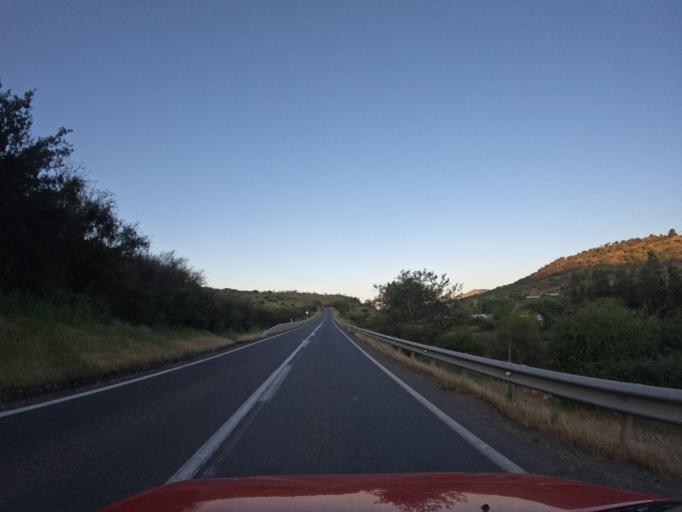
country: CL
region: Maule
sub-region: Provincia de Talca
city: Talca
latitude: -35.0782
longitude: -71.6325
